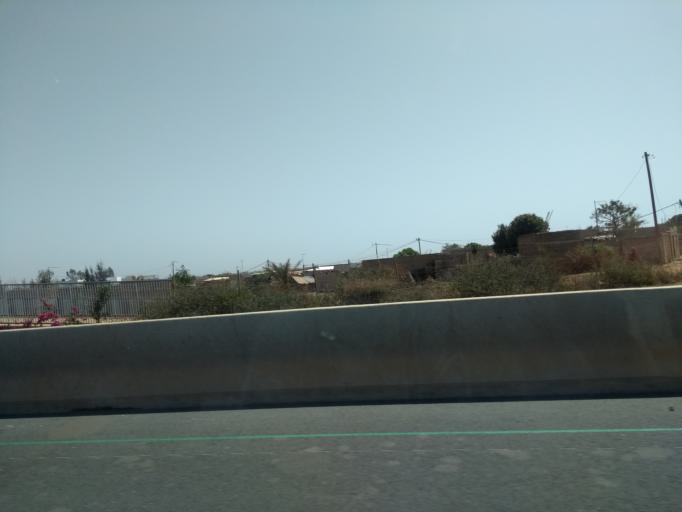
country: SN
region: Thies
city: Thies
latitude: 14.7359
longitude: -17.1784
